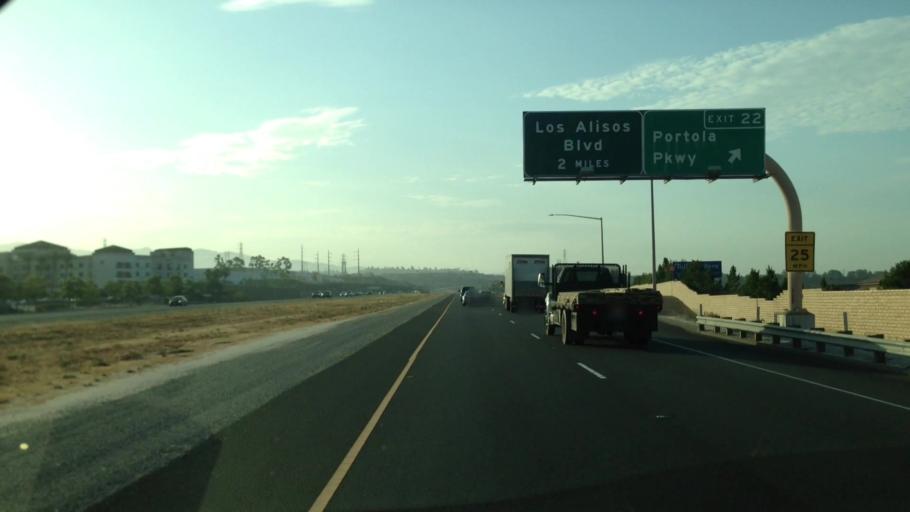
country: US
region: California
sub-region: Orange County
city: Foothill Ranch
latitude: 33.6698
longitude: -117.6559
